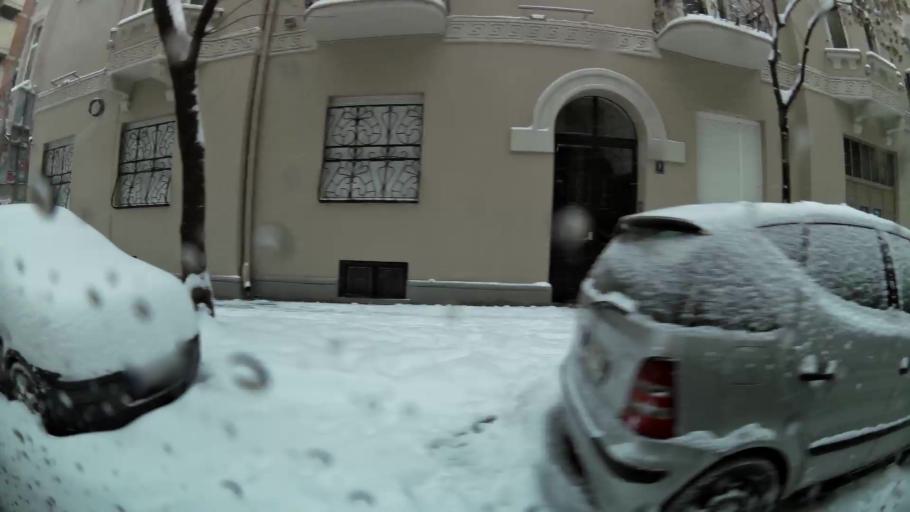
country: RS
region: Central Serbia
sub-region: Belgrade
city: Stari Grad
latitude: 44.8183
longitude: 20.4605
